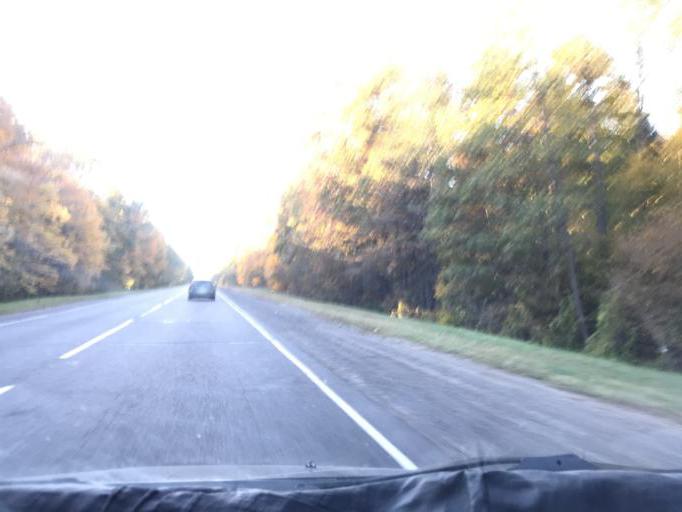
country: BY
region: Gomel
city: Pyetrykaw
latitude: 52.2727
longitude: 28.2647
